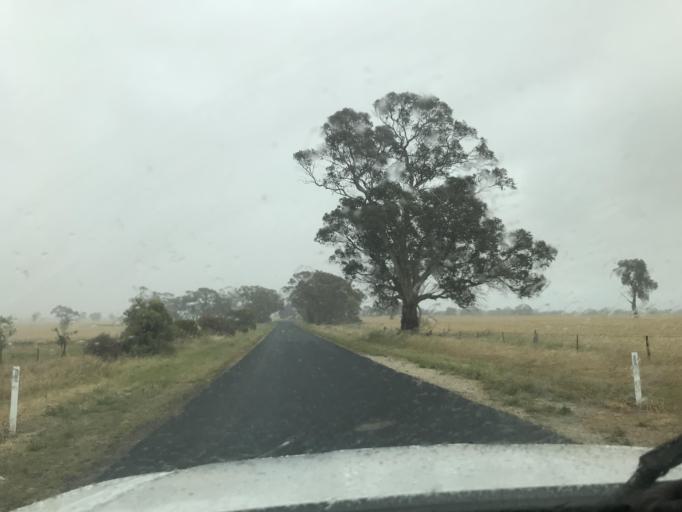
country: AU
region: South Australia
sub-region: Tatiara
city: Bordertown
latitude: -36.3280
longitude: 141.2103
